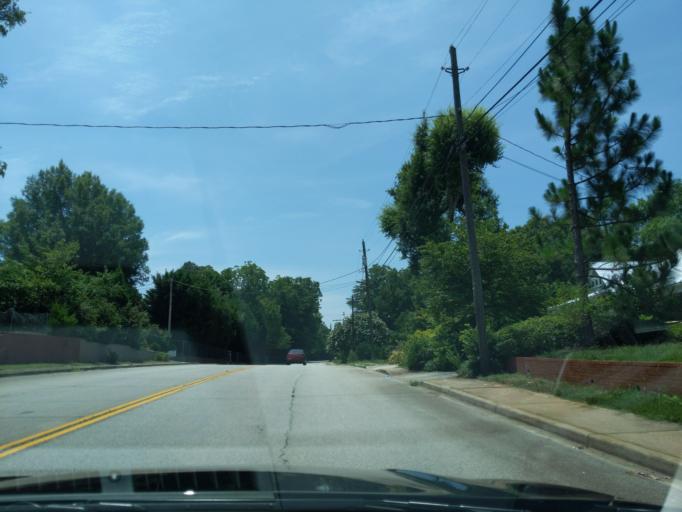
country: US
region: South Carolina
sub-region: Laurens County
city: Laurens
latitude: 34.4957
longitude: -82.0186
